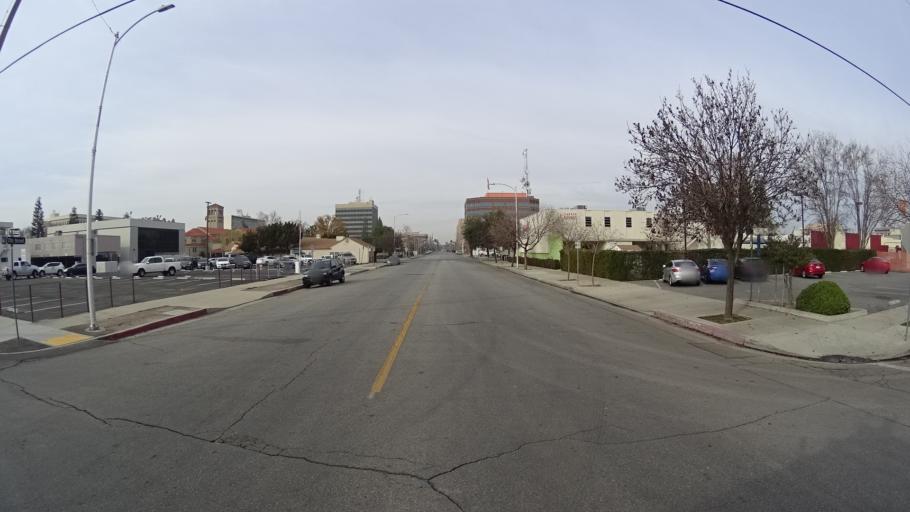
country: US
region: California
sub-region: Kern County
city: Bakersfield
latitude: 35.3743
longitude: -119.0141
